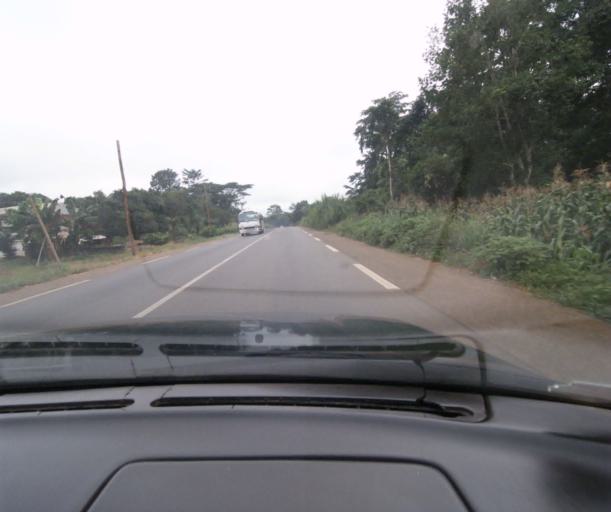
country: CM
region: Centre
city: Obala
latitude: 4.1926
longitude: 11.4532
